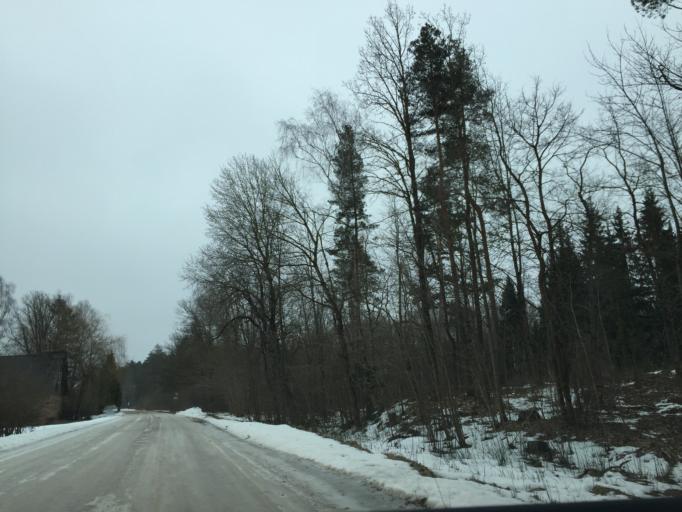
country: LV
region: Ozolnieku
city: Ozolnieki
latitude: 56.6311
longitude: 23.8112
